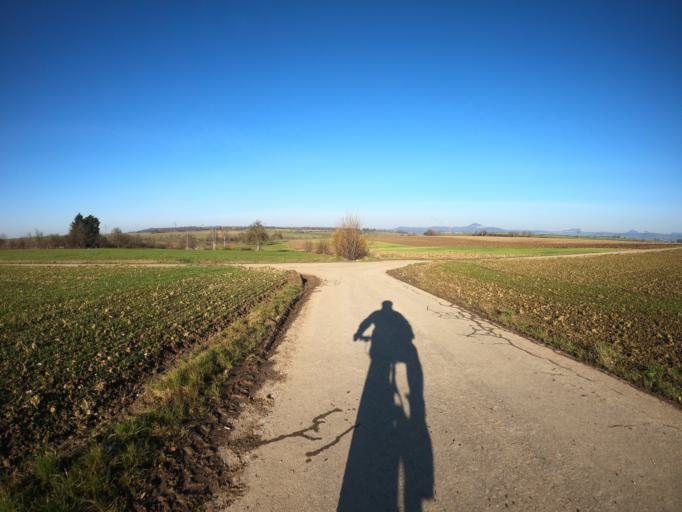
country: DE
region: Baden-Wuerttemberg
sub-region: Regierungsbezirk Stuttgart
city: Heiningen
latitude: 48.6666
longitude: 9.6629
